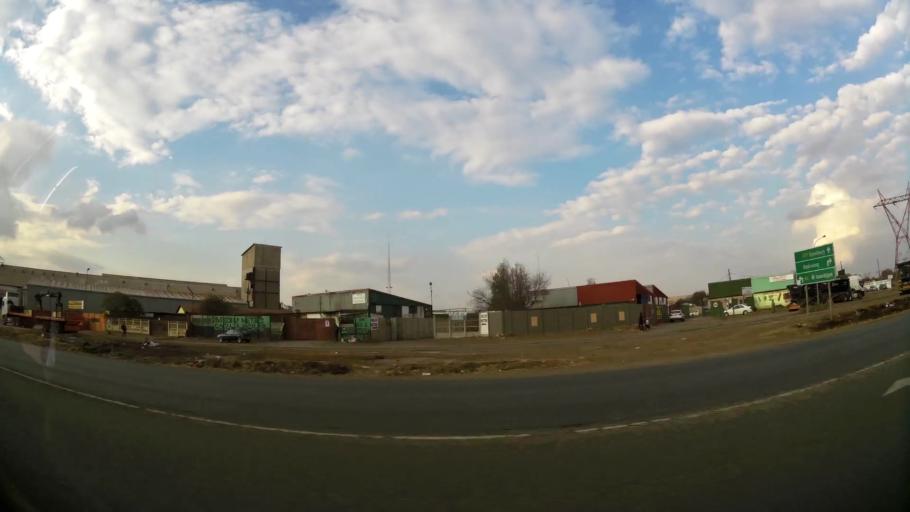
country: ZA
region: Gauteng
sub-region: Sedibeng District Municipality
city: Vanderbijlpark
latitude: -26.6889
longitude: 27.8020
